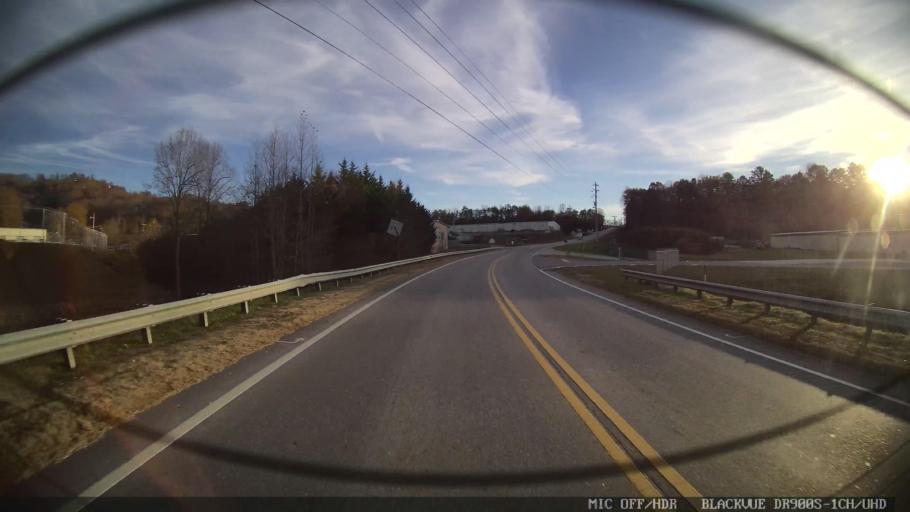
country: US
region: Georgia
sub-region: Union County
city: Blairsville
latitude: 34.8760
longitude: -83.9464
